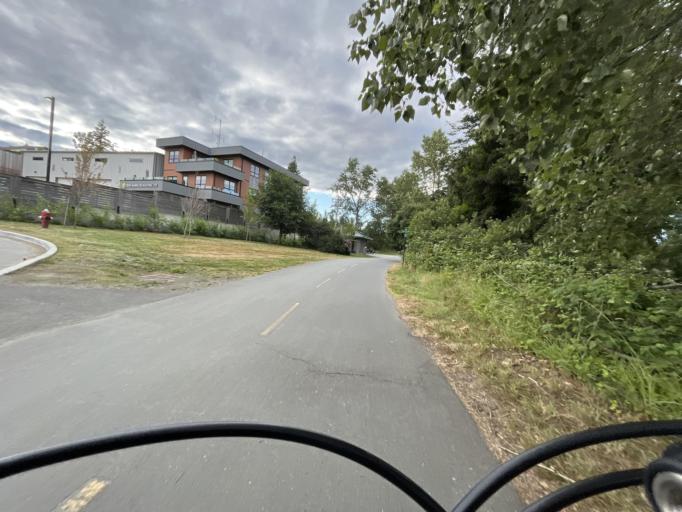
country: CA
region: British Columbia
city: Victoria
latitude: 48.4755
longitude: -123.3595
